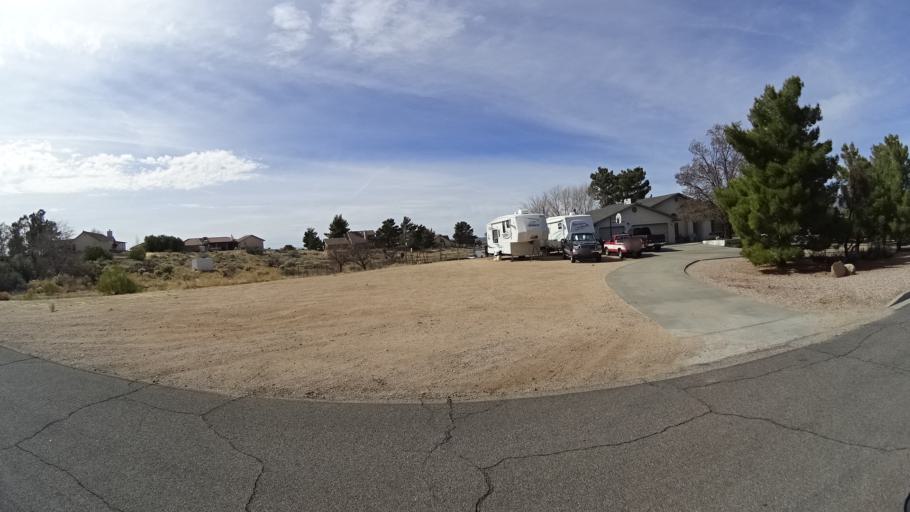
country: US
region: Arizona
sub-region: Mohave County
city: Kingman
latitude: 35.1827
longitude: -113.9885
